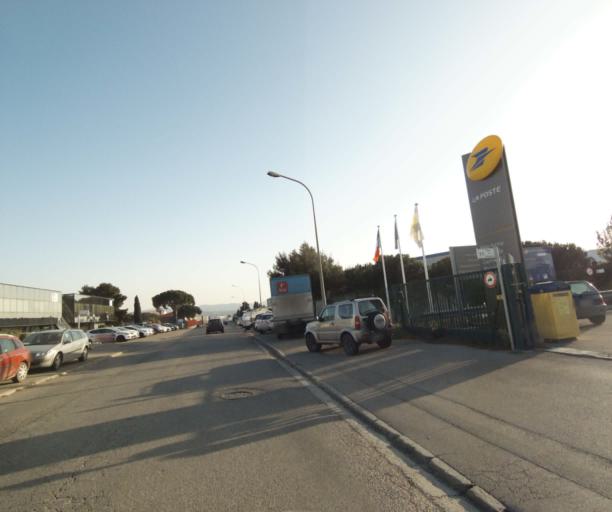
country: FR
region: Provence-Alpes-Cote d'Azur
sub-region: Departement des Bouches-du-Rhone
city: Saint-Victoret
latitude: 43.4355
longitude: 5.2395
